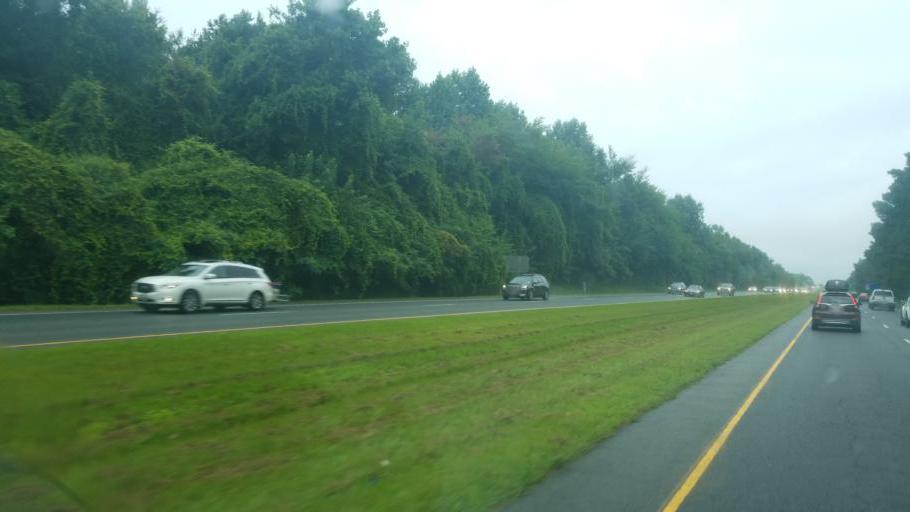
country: US
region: Virginia
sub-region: City of Chesapeake
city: Chesapeake
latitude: 36.6994
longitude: -76.2269
